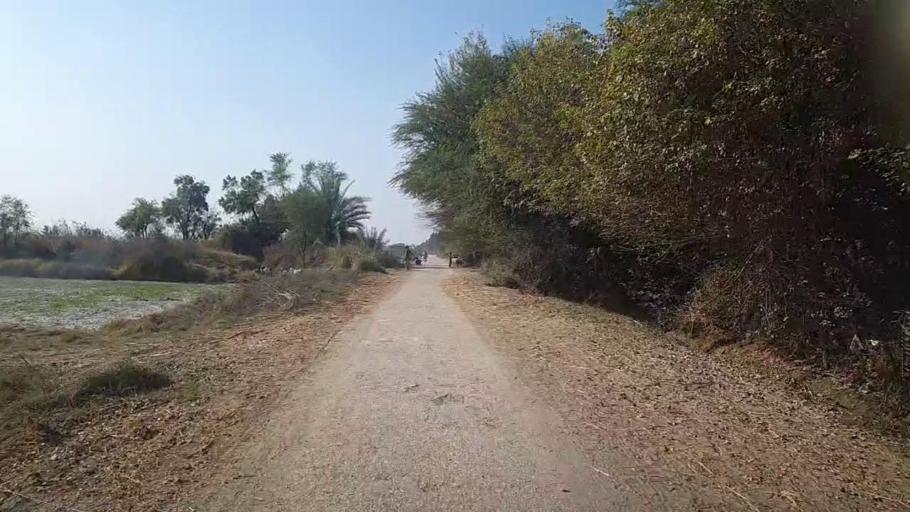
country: PK
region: Sindh
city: Mirpur Mathelo
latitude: 27.9009
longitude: 69.6374
